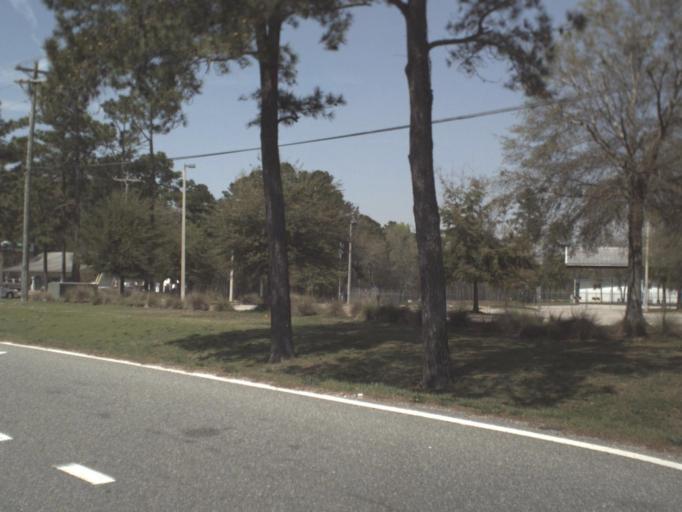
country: US
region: Florida
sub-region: Gadsden County
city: Midway
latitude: 30.4940
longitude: -84.4289
